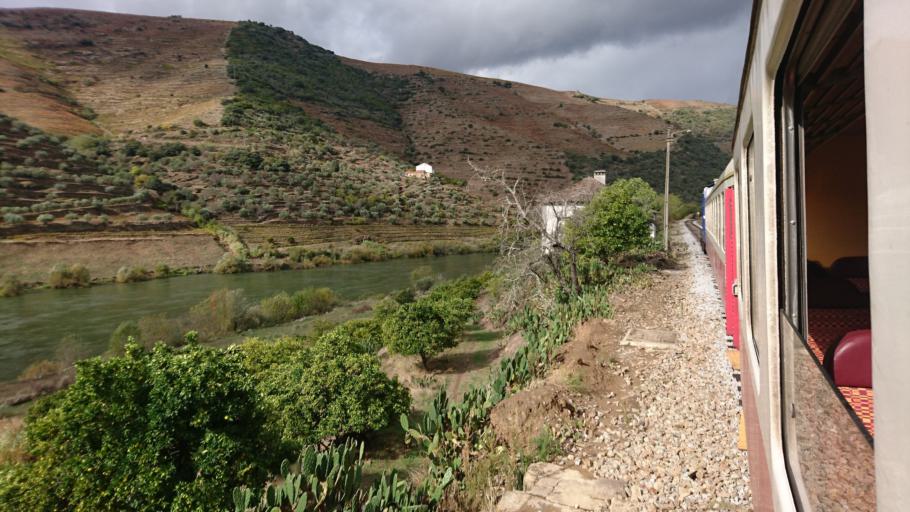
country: PT
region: Viseu
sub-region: Sao Joao da Pesqueira
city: Sao Joao da Pesqueira
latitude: 41.1765
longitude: -7.3786
